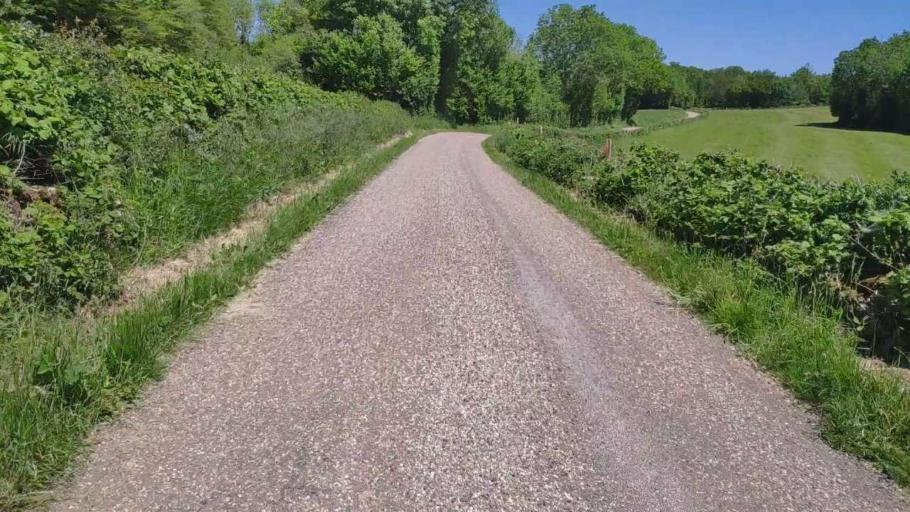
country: FR
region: Franche-Comte
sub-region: Departement du Jura
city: Perrigny
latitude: 46.7230
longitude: 5.6597
